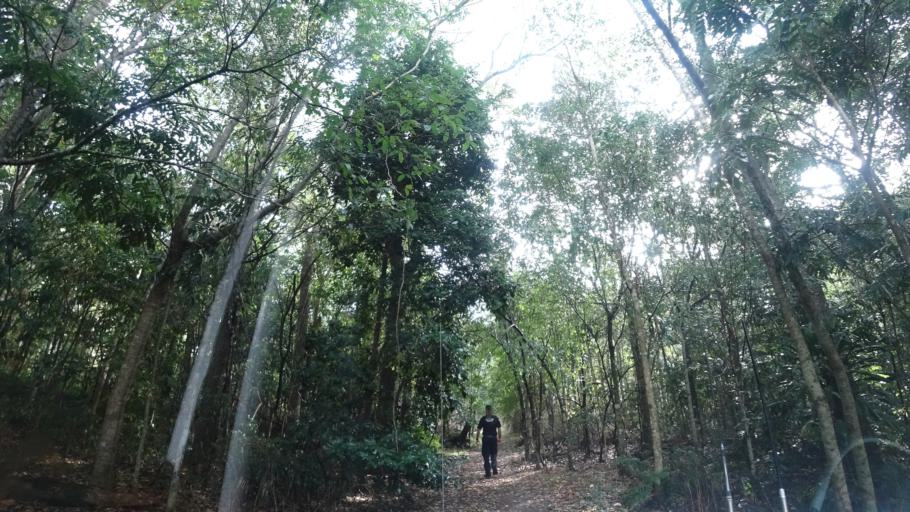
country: AU
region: Queensland
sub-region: Brisbane
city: Pullenvale
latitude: -27.4534
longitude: 152.8733
